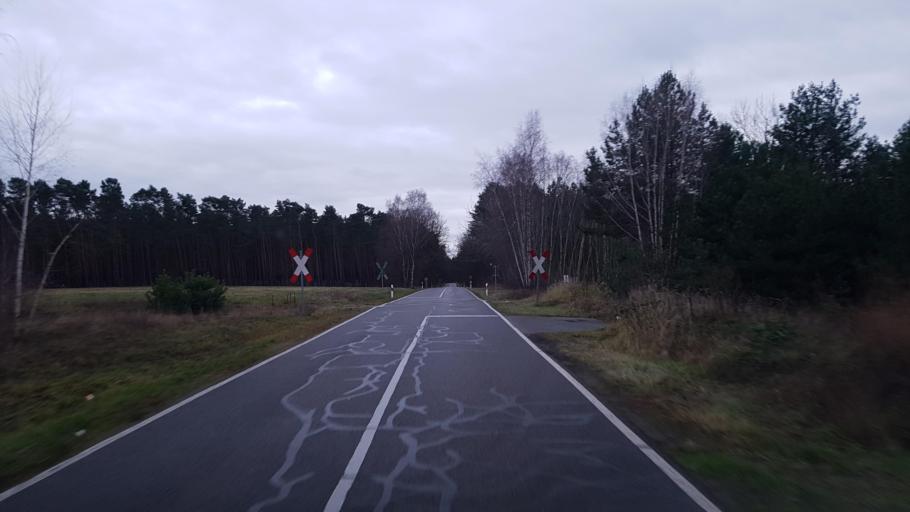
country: DE
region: Brandenburg
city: Schlepzig
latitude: 52.0178
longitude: 13.9776
